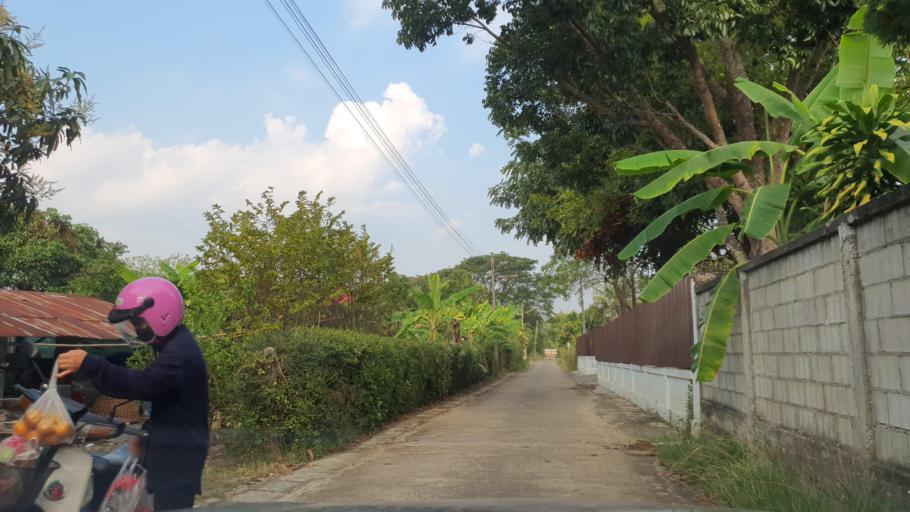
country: TH
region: Chiang Mai
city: San Kamphaeng
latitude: 18.7415
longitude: 99.1024
